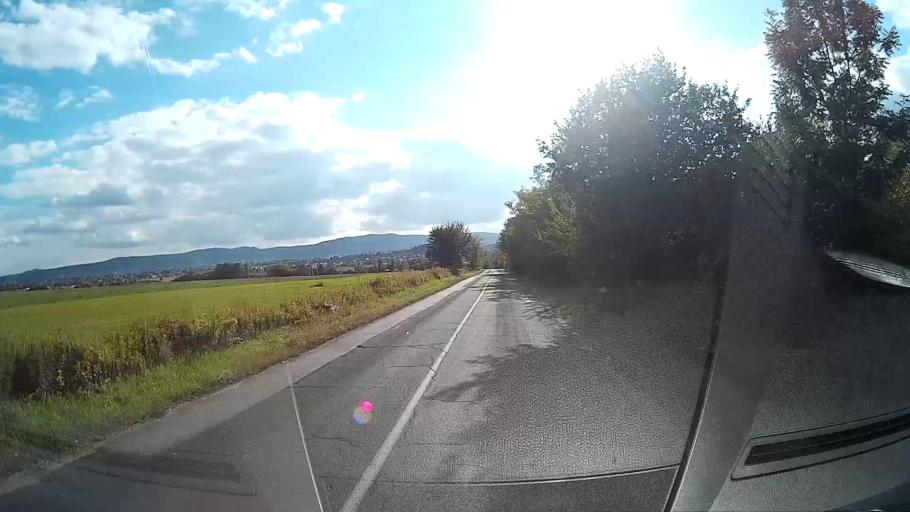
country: HU
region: Pest
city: Pilisvorosvar
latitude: 47.6398
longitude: 18.9076
